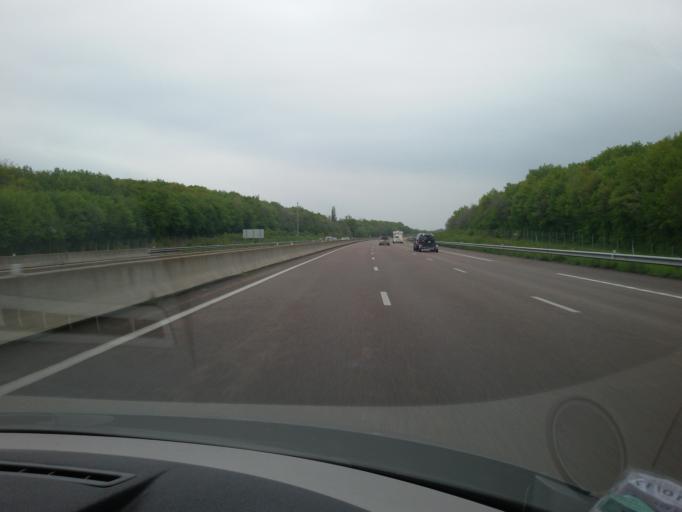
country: FR
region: Bourgogne
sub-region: Departement de la Cote-d'Or
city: Gevrey-Chambertin
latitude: 47.1943
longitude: 4.9966
